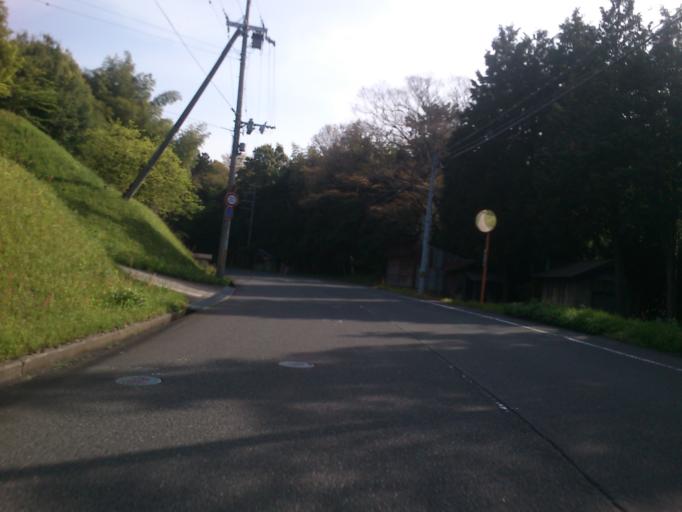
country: JP
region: Kyoto
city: Miyazu
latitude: 35.6137
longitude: 135.2250
